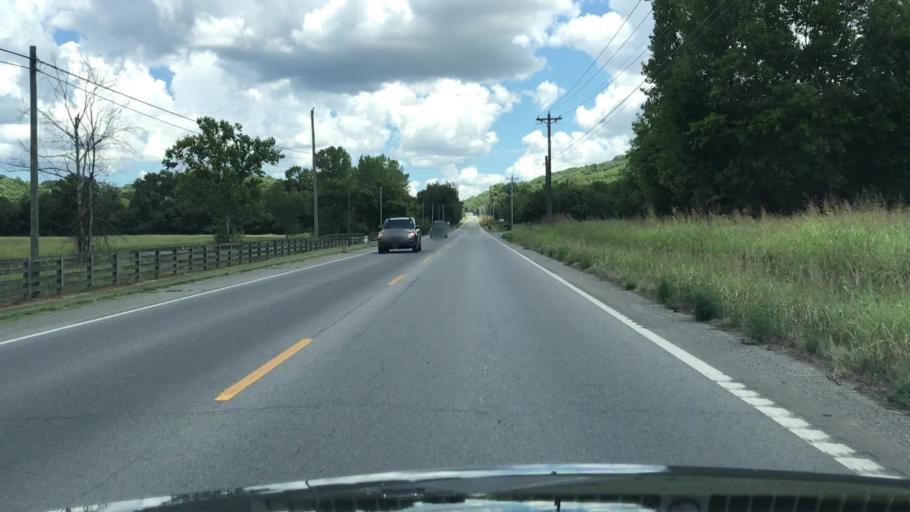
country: US
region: Tennessee
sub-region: Williamson County
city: Nolensville
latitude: 35.9092
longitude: -86.6627
